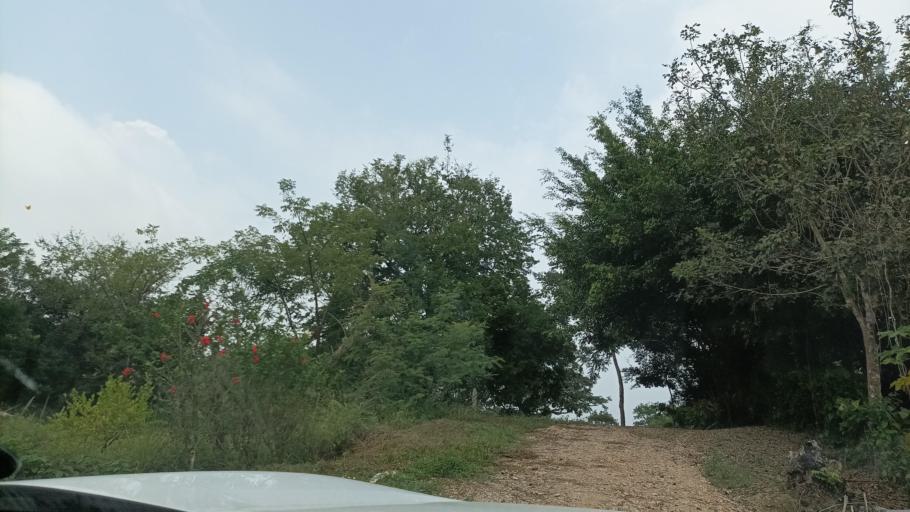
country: MX
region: Veracruz
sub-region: Moloacan
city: Cuichapa
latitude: 17.5829
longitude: -94.2349
